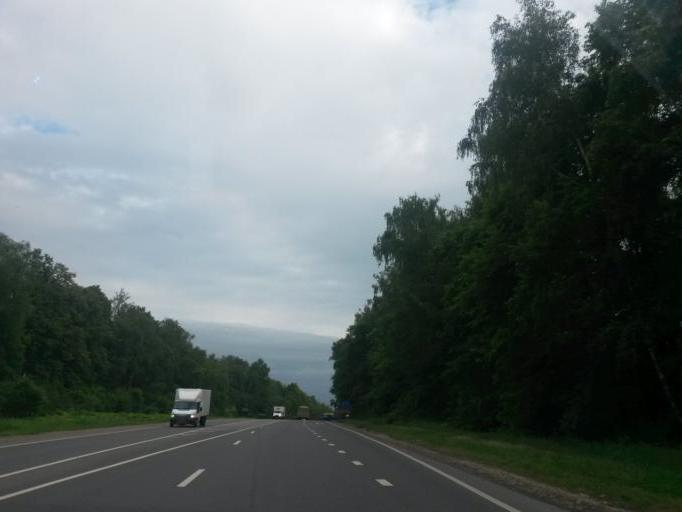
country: RU
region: Moskovskaya
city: Barybino
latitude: 55.2284
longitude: 37.8670
